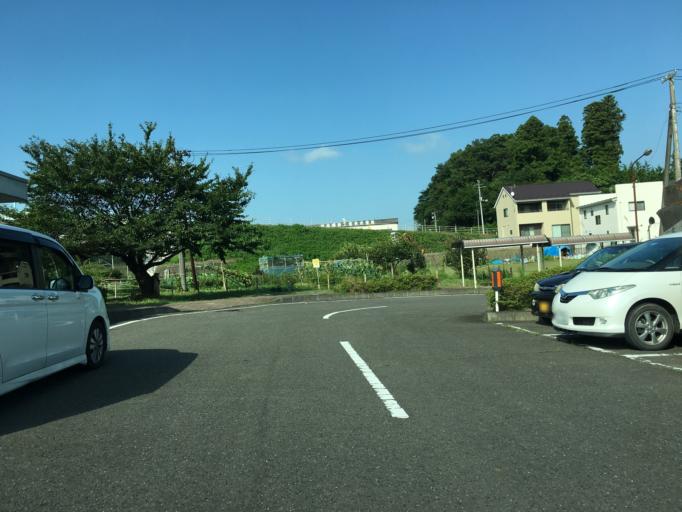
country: JP
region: Miyagi
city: Marumori
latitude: 37.9304
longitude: 140.7621
